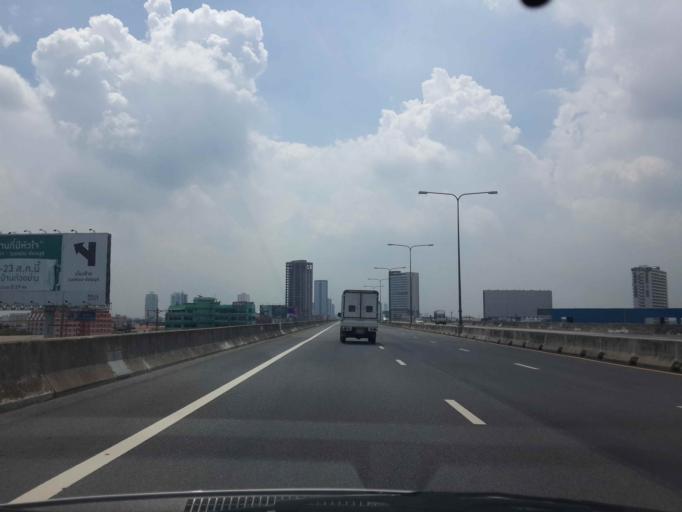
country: TH
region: Bangkok
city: Bang Na
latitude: 13.6717
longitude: 100.6148
